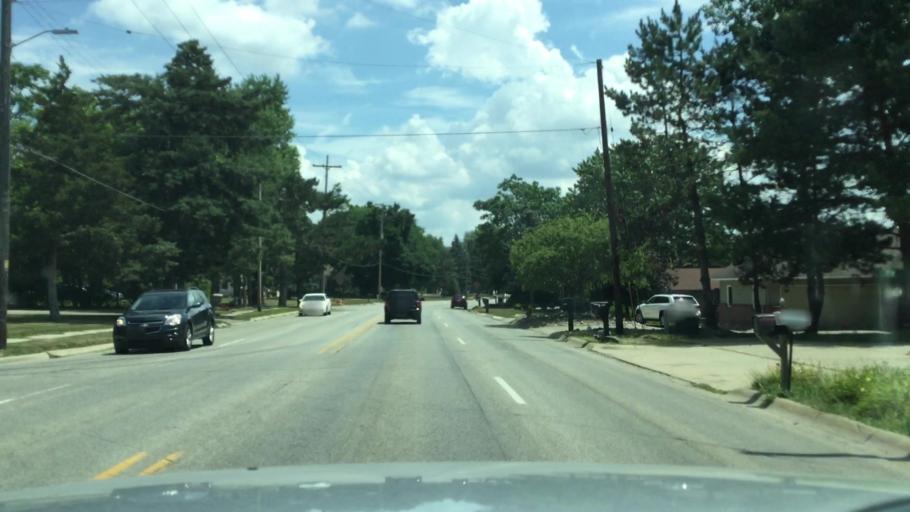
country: US
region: Michigan
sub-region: Genesee County
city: Flushing
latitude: 43.0624
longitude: -83.8276
